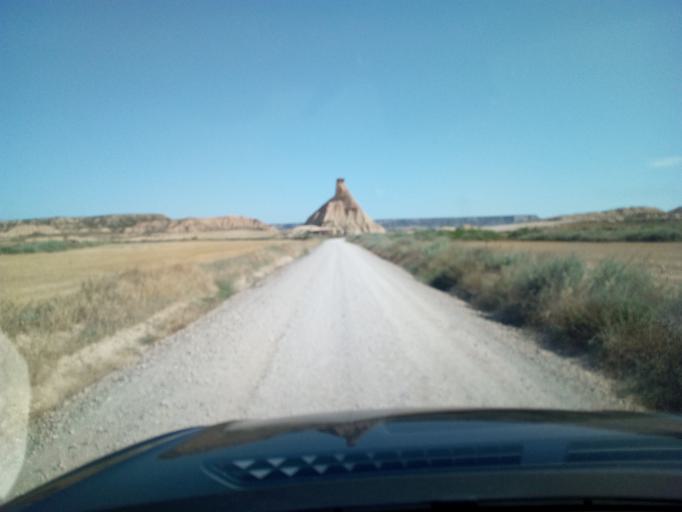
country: ES
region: Navarre
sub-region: Provincia de Navarra
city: Arguedas
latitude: 42.2074
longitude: -1.5160
